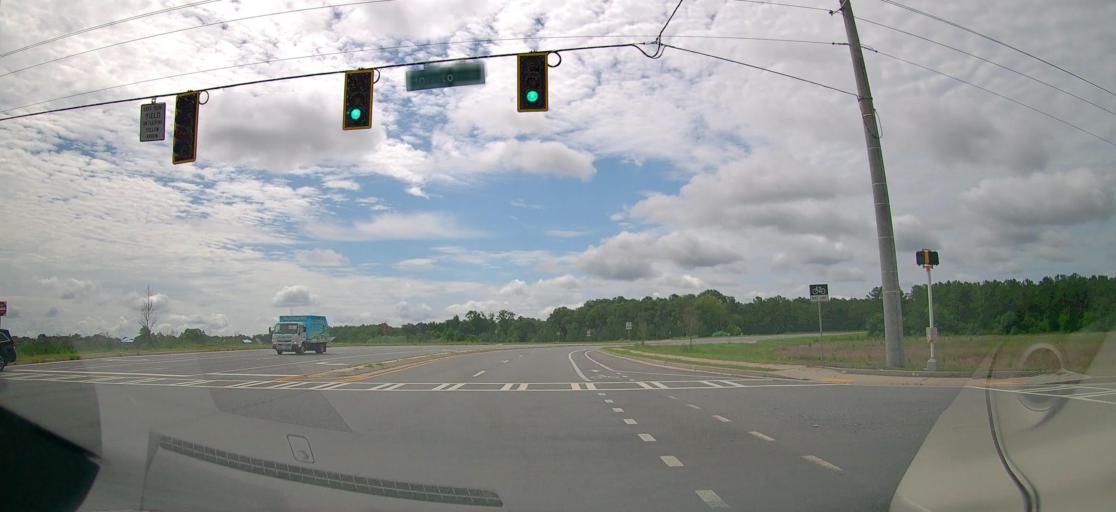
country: US
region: Georgia
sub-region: Houston County
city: Centerville
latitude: 32.7106
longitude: -83.6956
